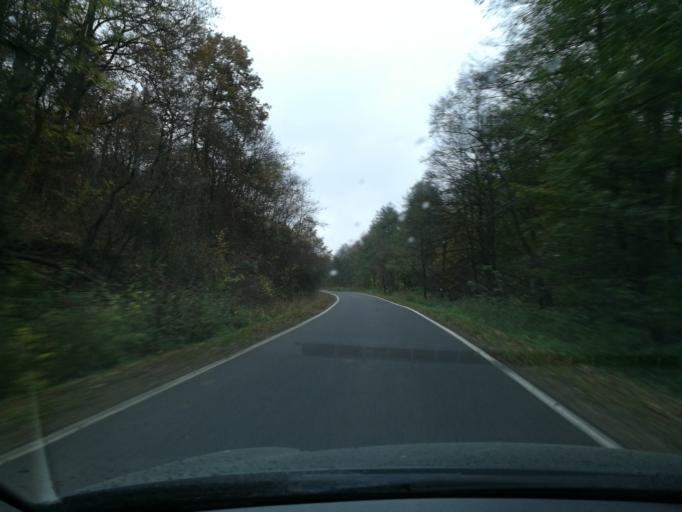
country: HU
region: Nograd
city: Paszto
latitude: 47.9696
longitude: 19.6219
